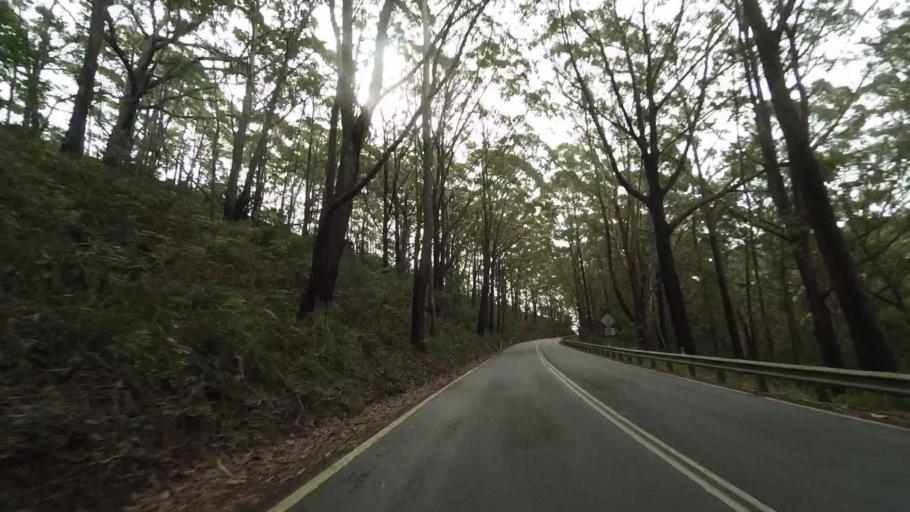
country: AU
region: New South Wales
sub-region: Wollongong
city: Helensburgh
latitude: -34.2182
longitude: 151.0014
